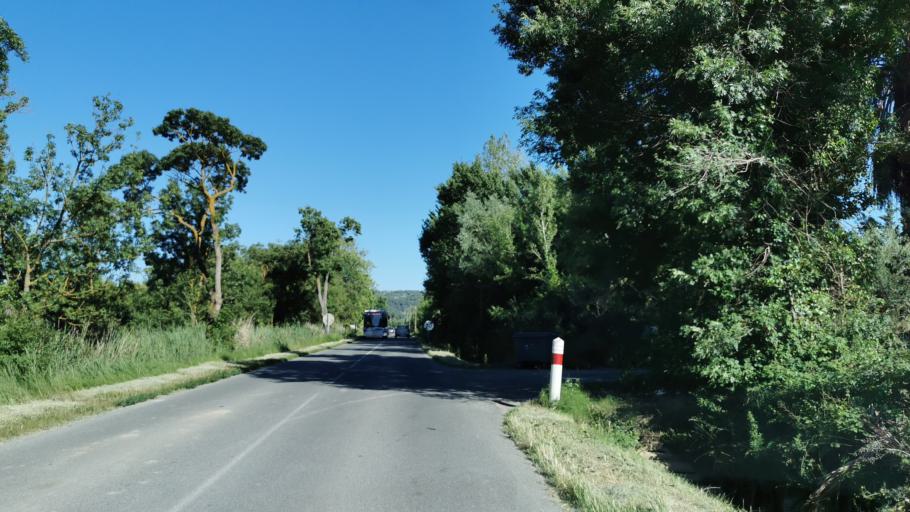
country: FR
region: Languedoc-Roussillon
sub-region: Departement de l'Aude
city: Narbonne
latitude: 43.1682
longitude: 3.0392
